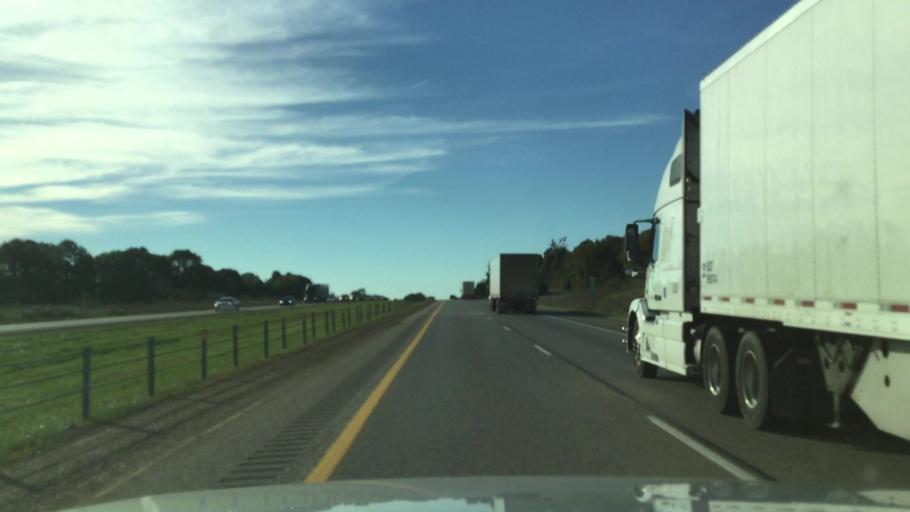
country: US
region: Michigan
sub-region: Calhoun County
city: Springfield
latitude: 42.2750
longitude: -85.3079
